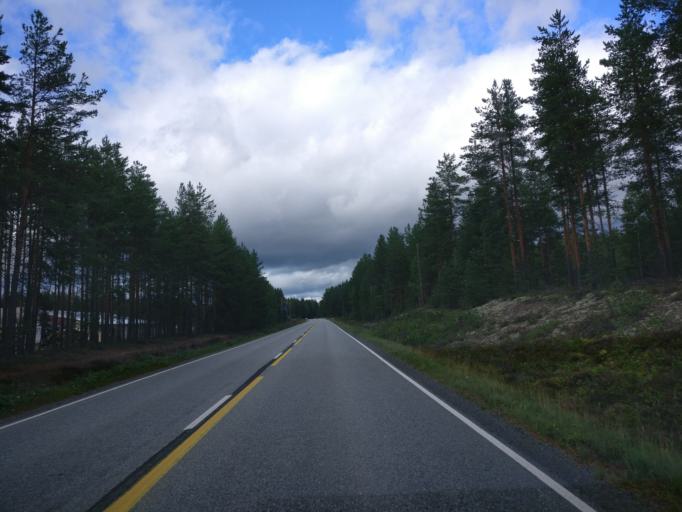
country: FI
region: Central Finland
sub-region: Jyvaeskylae
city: Toivakka
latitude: 62.1241
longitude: 26.1006
